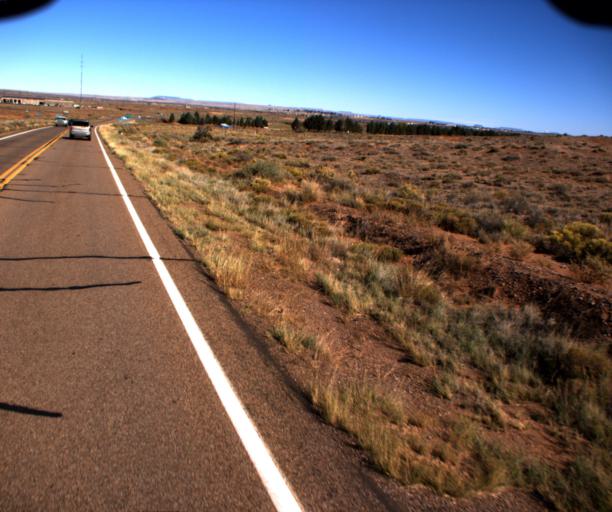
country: US
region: Arizona
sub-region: Navajo County
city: Holbrook
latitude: 34.8643
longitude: -110.1575
